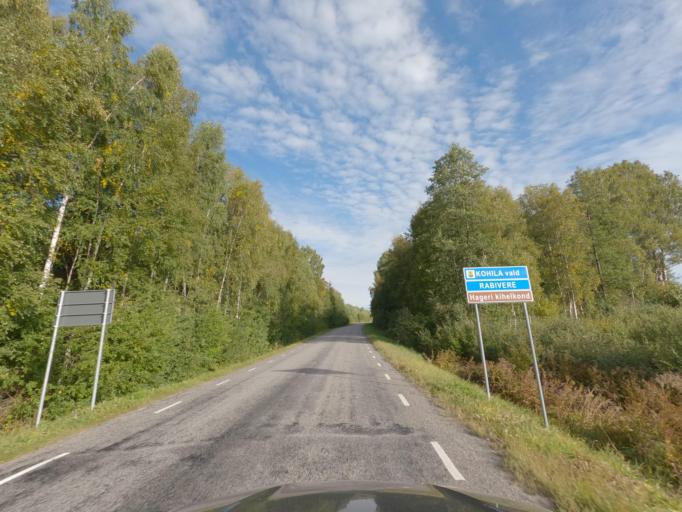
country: EE
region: Raplamaa
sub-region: Kohila vald
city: Kohila
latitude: 59.0841
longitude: 24.6754
